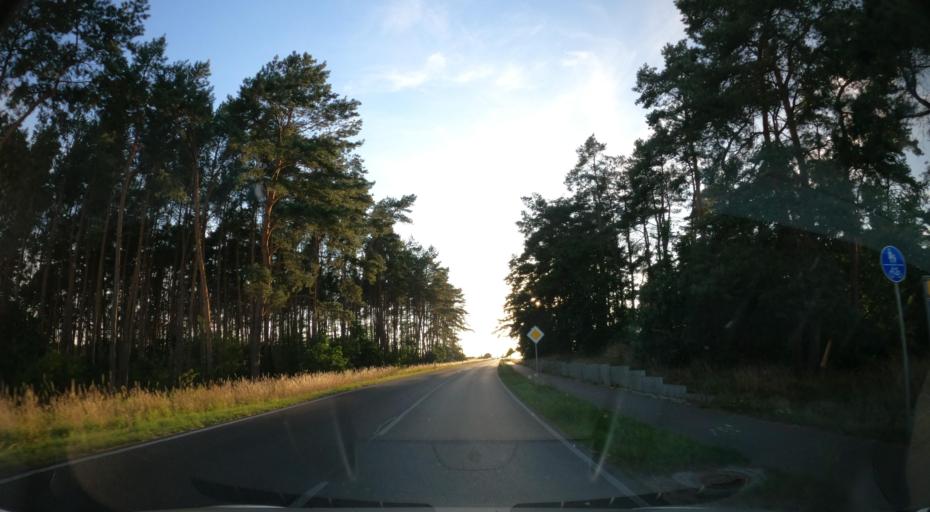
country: PL
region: West Pomeranian Voivodeship
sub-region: Powiat policki
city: Dobra
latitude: 53.4558
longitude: 14.2717
